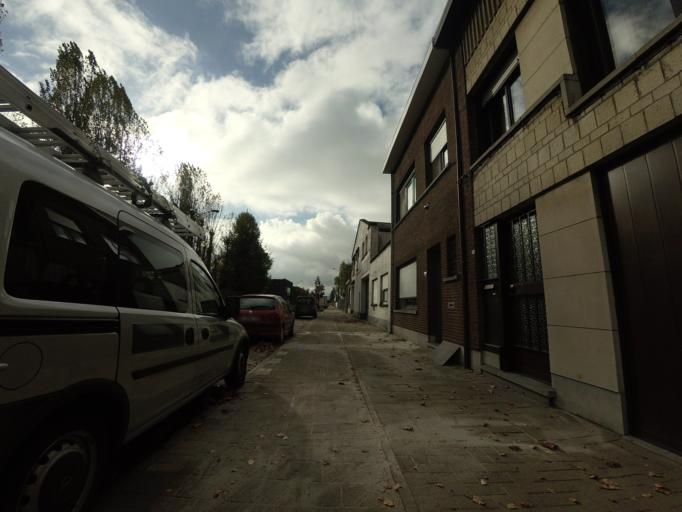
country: BE
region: Flanders
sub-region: Provincie Antwerpen
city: Schoten
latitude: 51.2424
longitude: 4.4586
